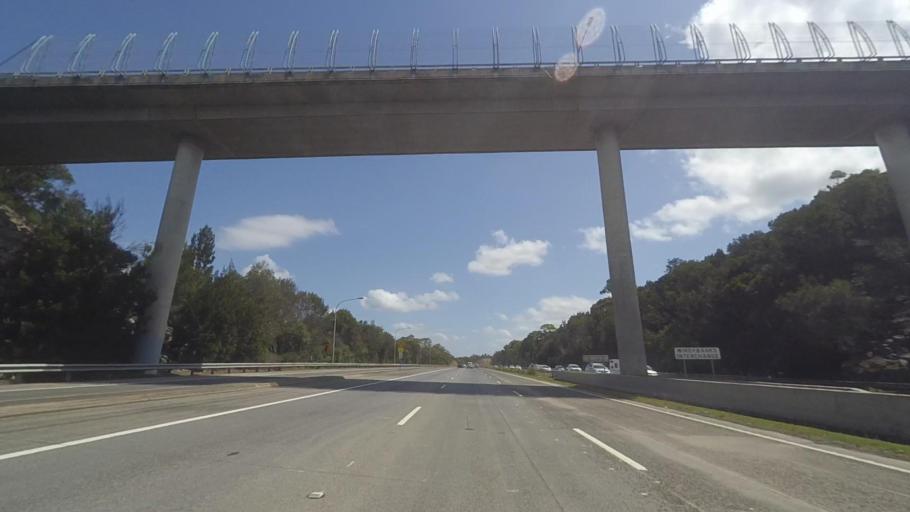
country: AU
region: New South Wales
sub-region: Hornsby Shire
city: Berowra
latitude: -33.6359
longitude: 151.1478
